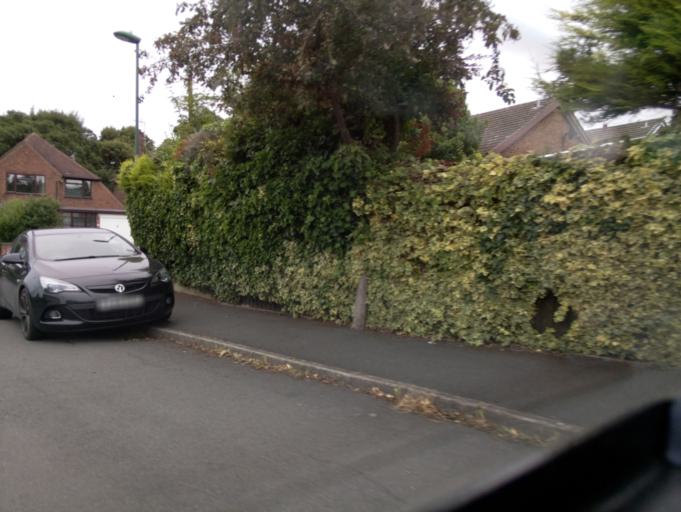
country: GB
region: England
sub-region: Nottinghamshire
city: Arnold
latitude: 52.9833
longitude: -1.1304
